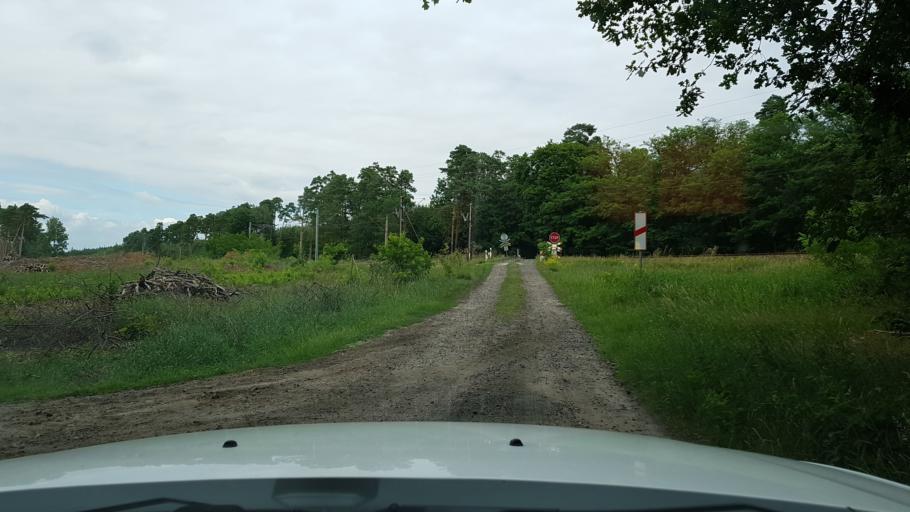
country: PL
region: West Pomeranian Voivodeship
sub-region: Powiat mysliborski
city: Boleszkowice
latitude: 52.6646
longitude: 14.5800
